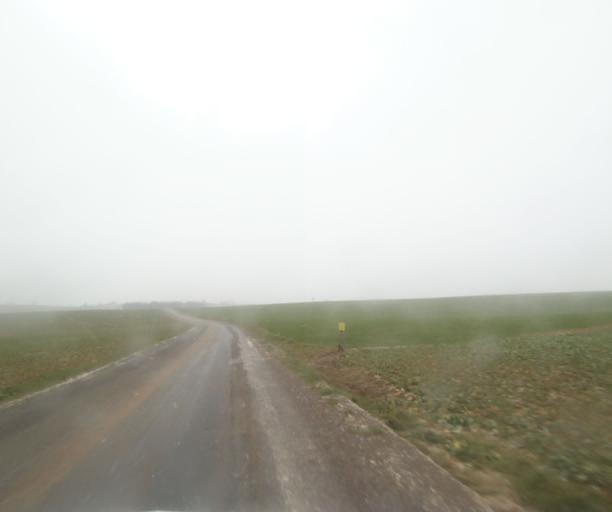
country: FR
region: Champagne-Ardenne
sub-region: Departement de la Haute-Marne
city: Bienville
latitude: 48.5371
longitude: 5.0590
